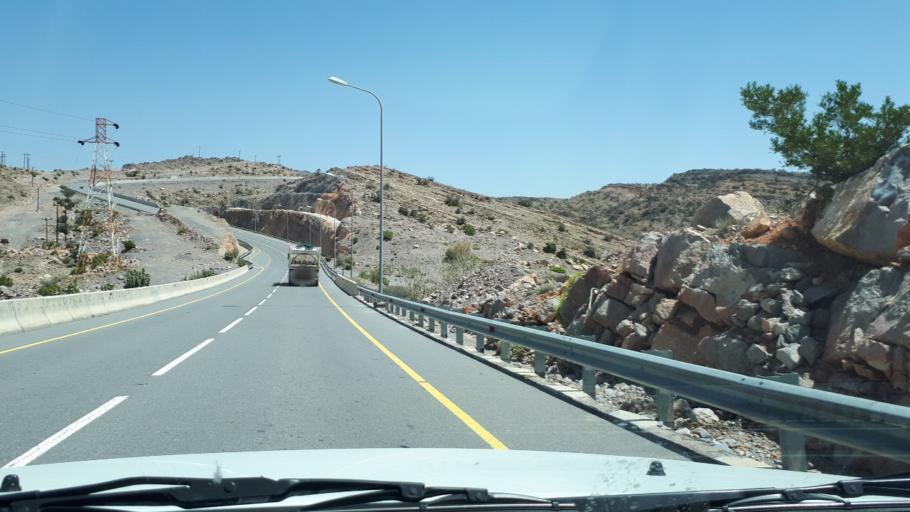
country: OM
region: Muhafazat ad Dakhiliyah
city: Izki
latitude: 23.0328
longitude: 57.7045
